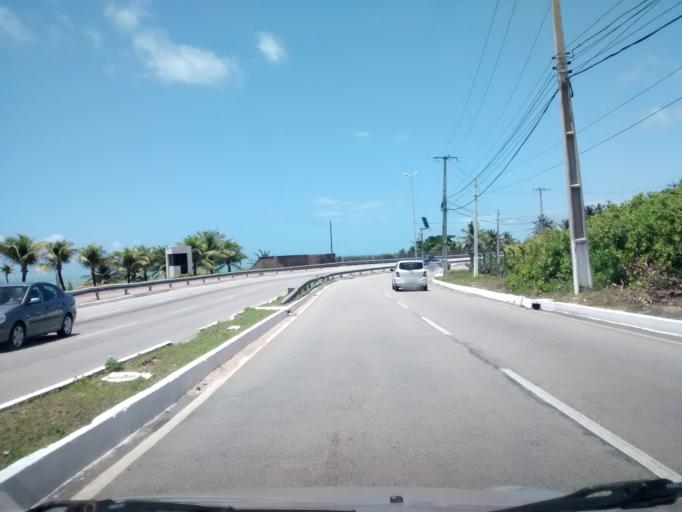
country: BR
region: Rio Grande do Norte
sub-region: Natal
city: Natal
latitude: -5.8045
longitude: -35.1824
